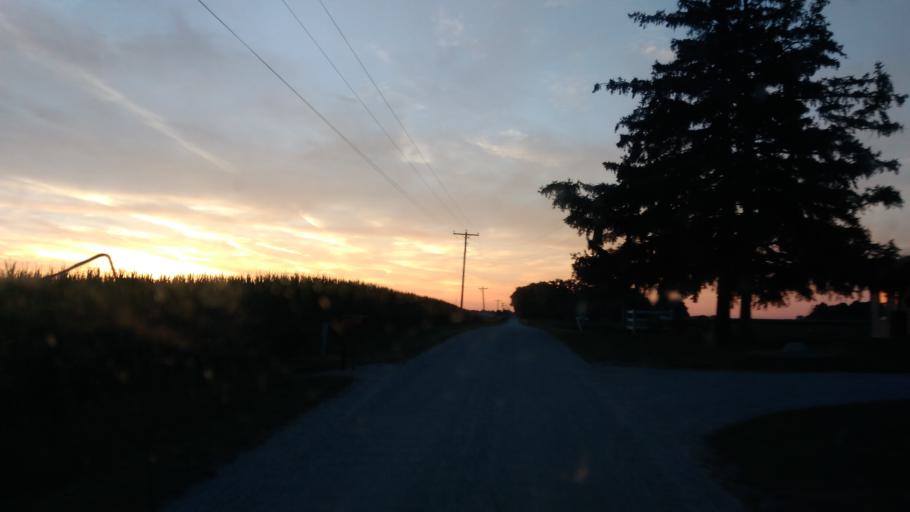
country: US
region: Indiana
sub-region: Wells County
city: Bluffton
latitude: 40.6844
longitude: -85.1310
